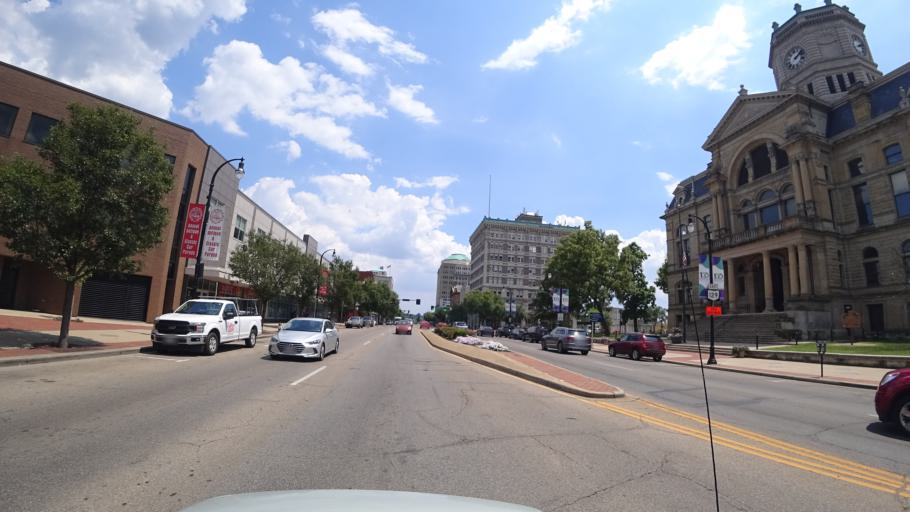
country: US
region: Ohio
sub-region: Butler County
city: Hamilton
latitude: 39.4001
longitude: -84.5629
